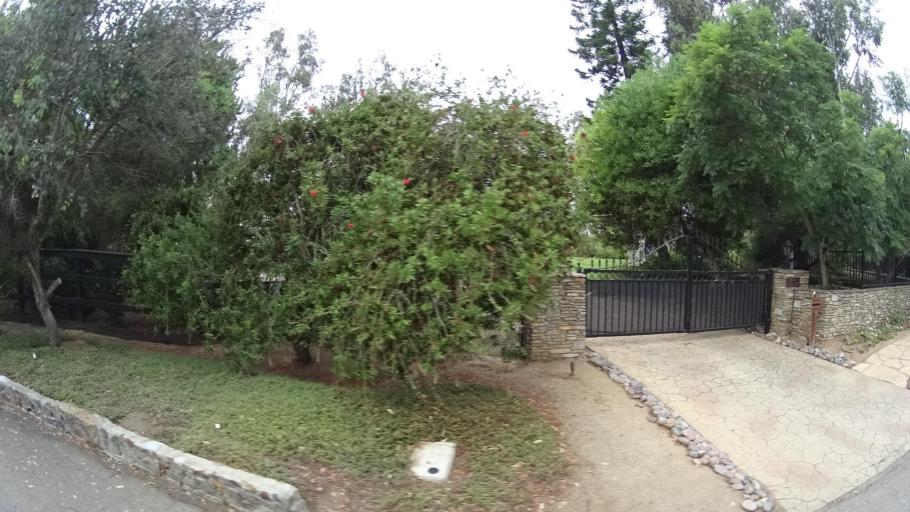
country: US
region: California
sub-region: San Diego County
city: Solana Beach
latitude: 32.9958
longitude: -117.2370
